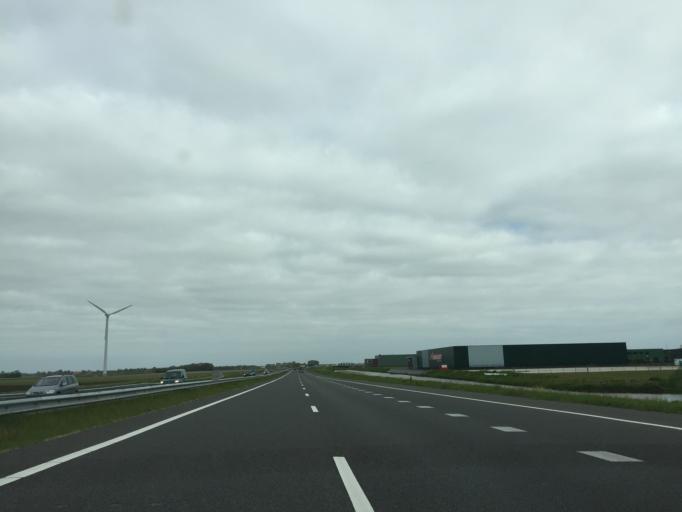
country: NL
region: North Holland
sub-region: Gemeente Medemblik
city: Opperdoes
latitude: 52.7534
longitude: 5.0339
